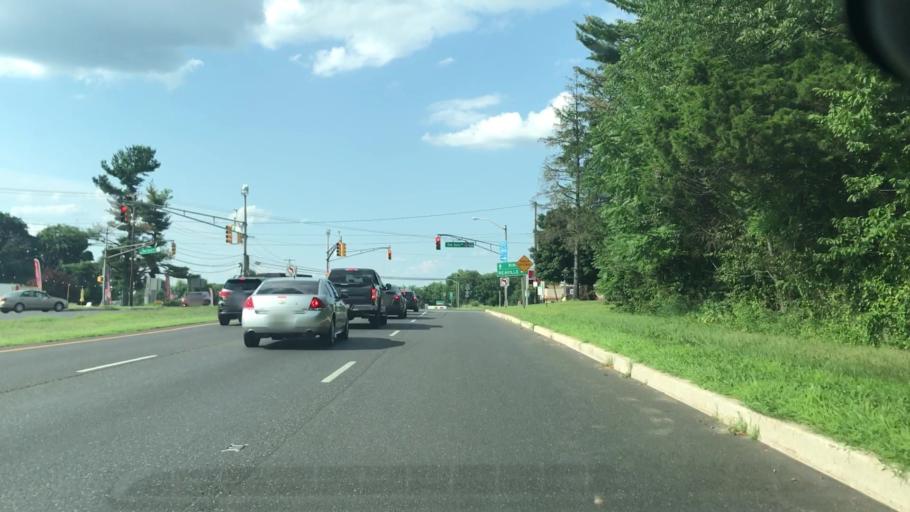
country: US
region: New Jersey
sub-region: Hunterdon County
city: Flemington
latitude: 40.4396
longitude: -74.8580
